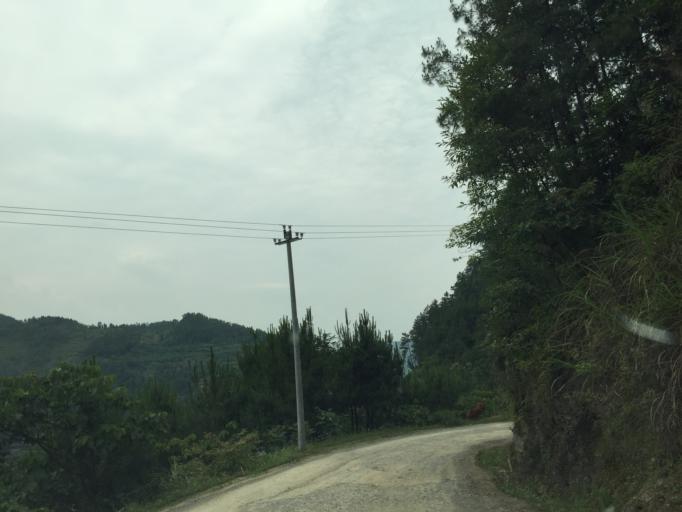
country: CN
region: Guizhou Sheng
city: Tongjing
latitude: 28.3706
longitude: 108.2537
